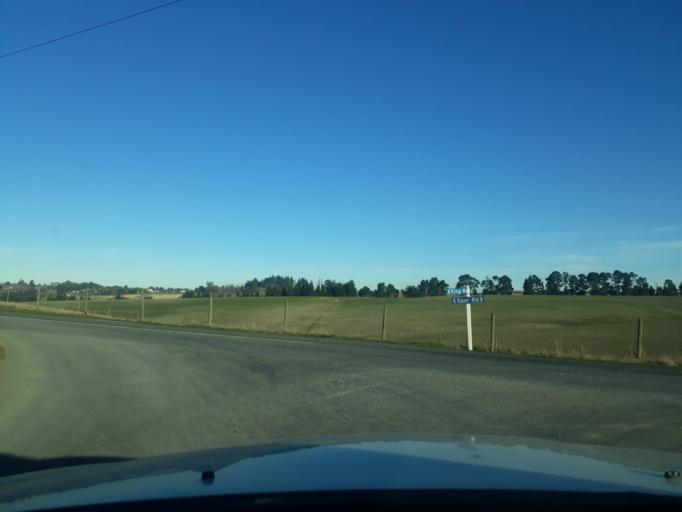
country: NZ
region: Canterbury
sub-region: Timaru District
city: Pleasant Point
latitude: -44.3550
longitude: 171.1560
